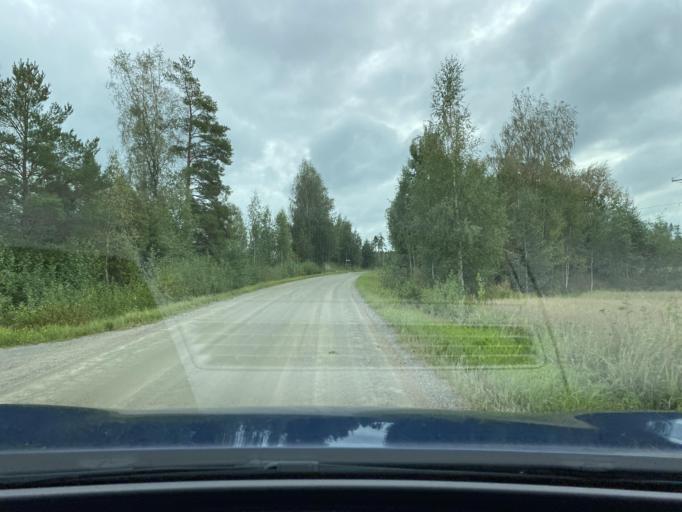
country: FI
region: Pirkanmaa
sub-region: Lounais-Pirkanmaa
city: Punkalaidun
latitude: 61.2164
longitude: 23.1681
